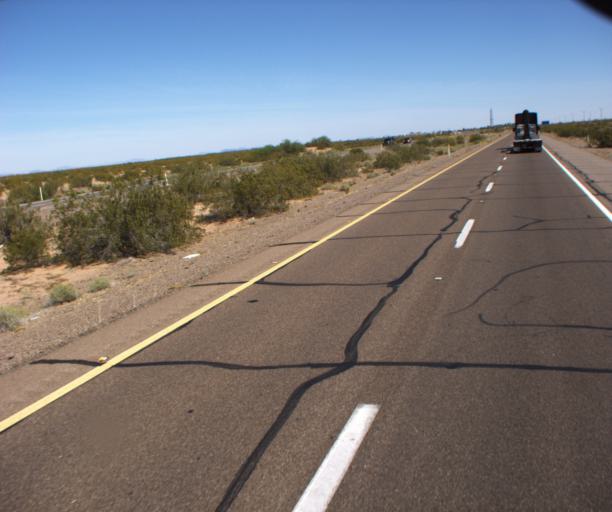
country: US
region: Arizona
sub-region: Yuma County
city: Wellton
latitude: 32.7877
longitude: -113.5640
